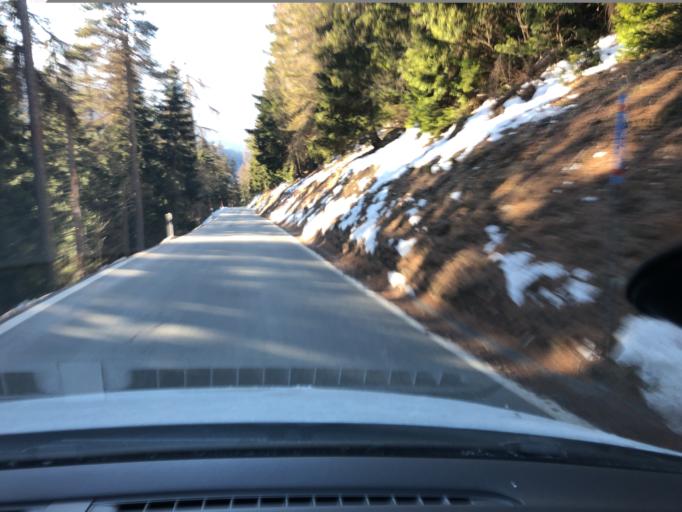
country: CH
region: Valais
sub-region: Goms District
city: Fiesch
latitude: 46.4150
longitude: 8.1505
